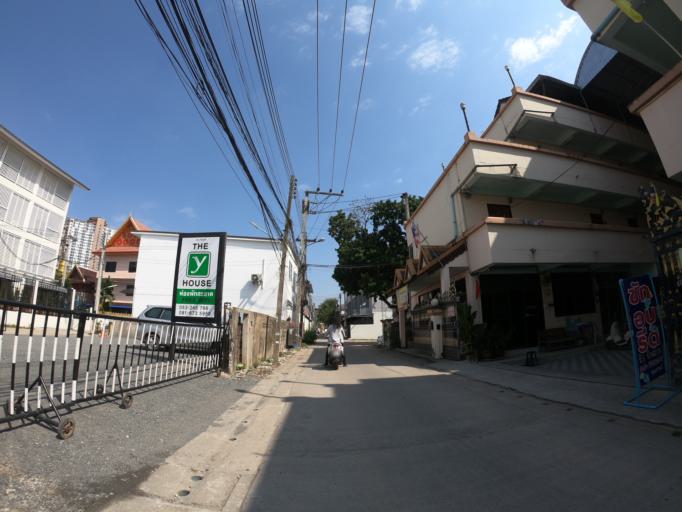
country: TH
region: Chiang Mai
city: Chiang Mai
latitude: 18.7981
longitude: 99.0178
